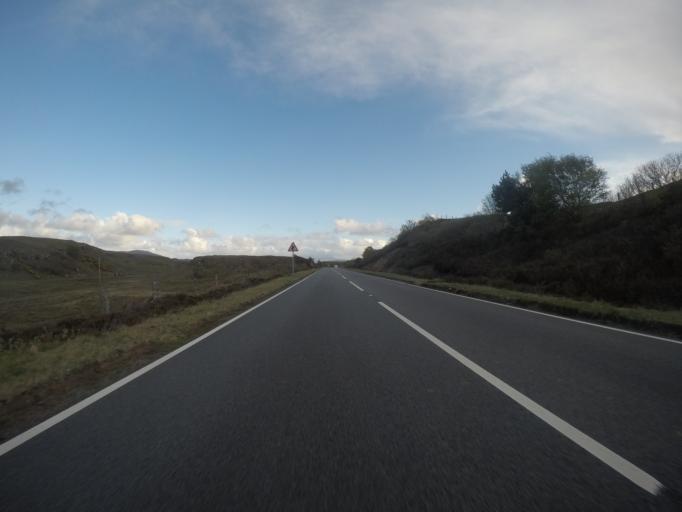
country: GB
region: Scotland
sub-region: Highland
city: Portree
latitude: 57.5145
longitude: -6.3413
